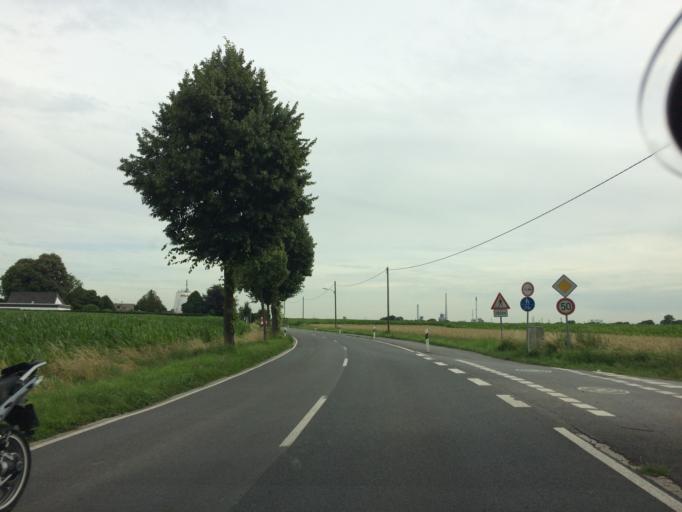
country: DE
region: North Rhine-Westphalia
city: Marl
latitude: 51.7215
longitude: 7.0879
